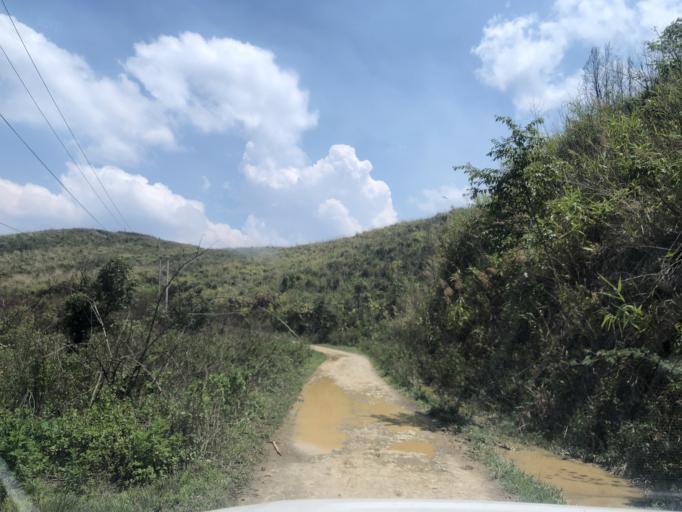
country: LA
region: Phongsali
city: Phongsali
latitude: 21.4039
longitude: 102.1860
